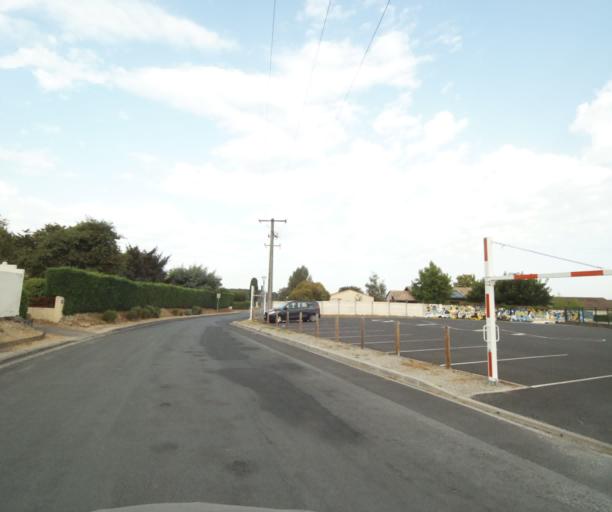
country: FR
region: Aquitaine
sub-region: Departement de la Gironde
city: Creon
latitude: 44.7720
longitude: -0.3542
